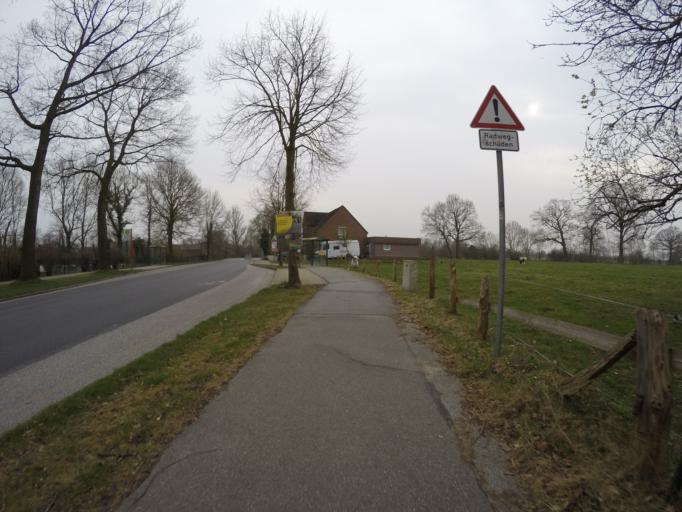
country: DE
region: Schleswig-Holstein
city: Borstel-Hohenraden
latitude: 53.7027
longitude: 9.8295
